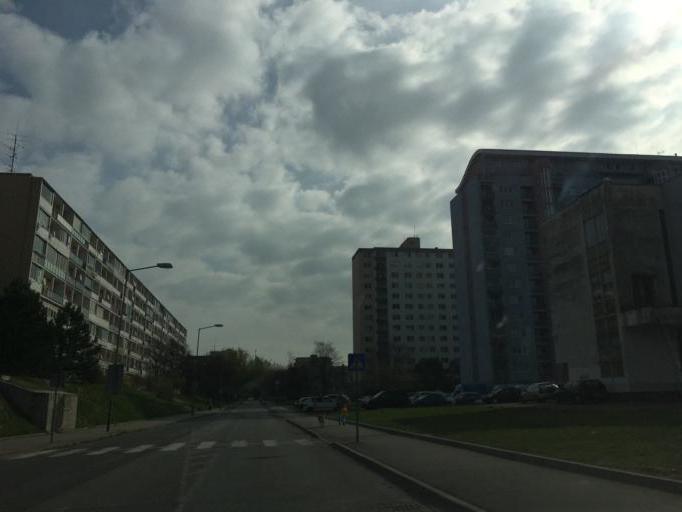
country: SK
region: Bratislavsky
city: Bratislava
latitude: 48.1524
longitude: 17.1586
